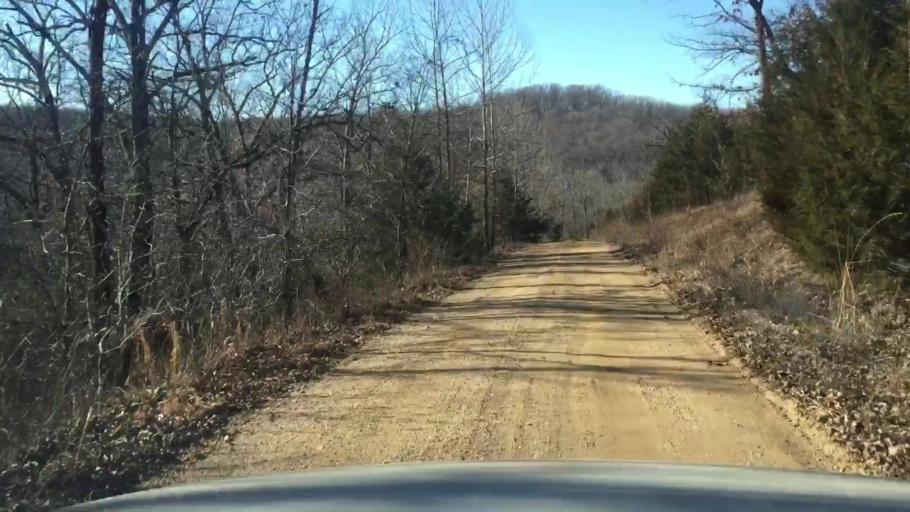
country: US
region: Missouri
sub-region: Camden County
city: Four Seasons
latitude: 38.3200
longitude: -92.7617
